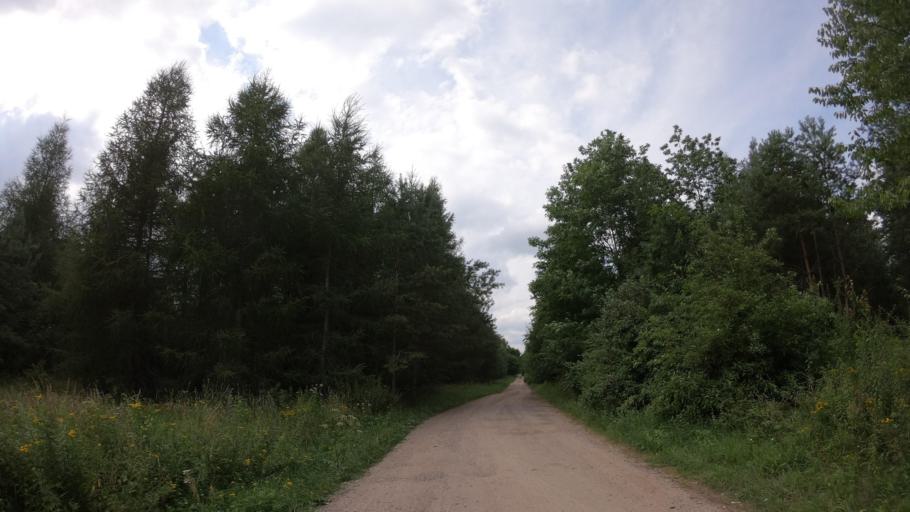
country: PL
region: West Pomeranian Voivodeship
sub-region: Powiat drawski
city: Kalisz Pomorski
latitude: 53.2833
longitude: 15.9406
